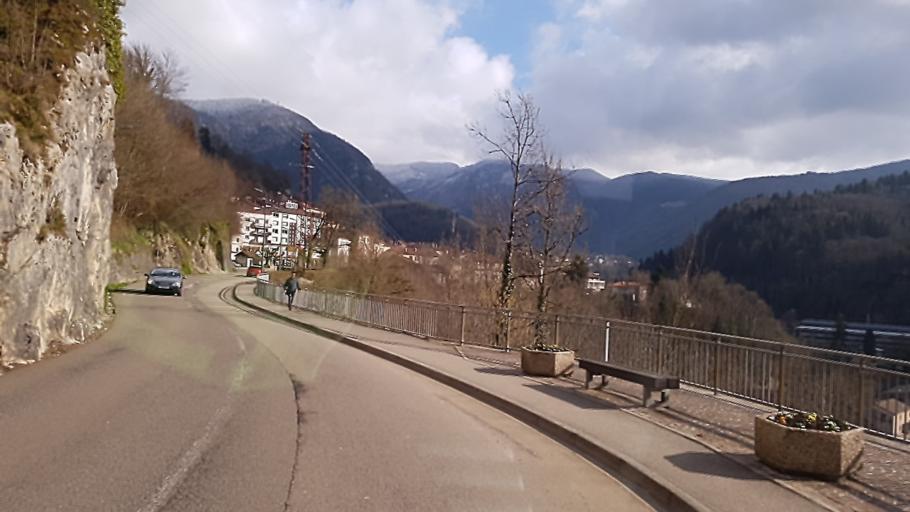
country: FR
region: Franche-Comte
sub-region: Departement du Jura
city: Saint-Claude
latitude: 46.3855
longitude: 5.8683
